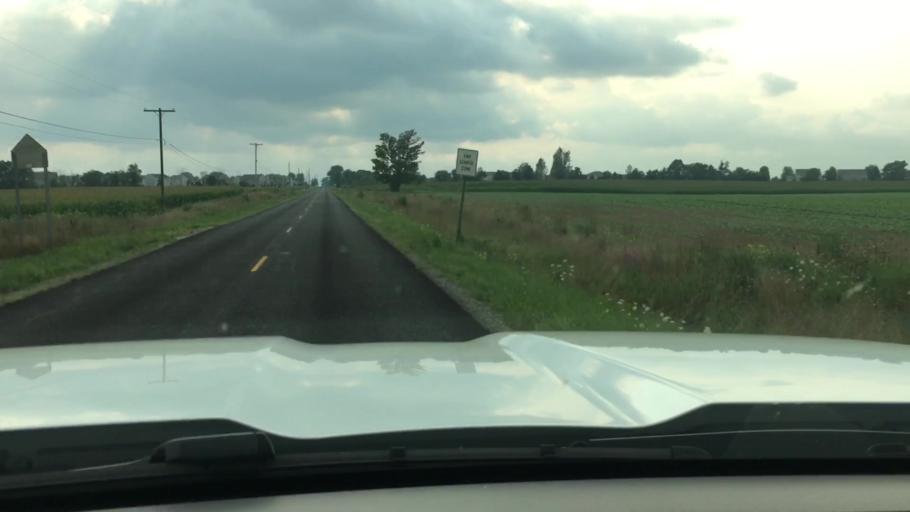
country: US
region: Michigan
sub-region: Ottawa County
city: Hudsonville
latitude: 42.8330
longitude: -85.8470
